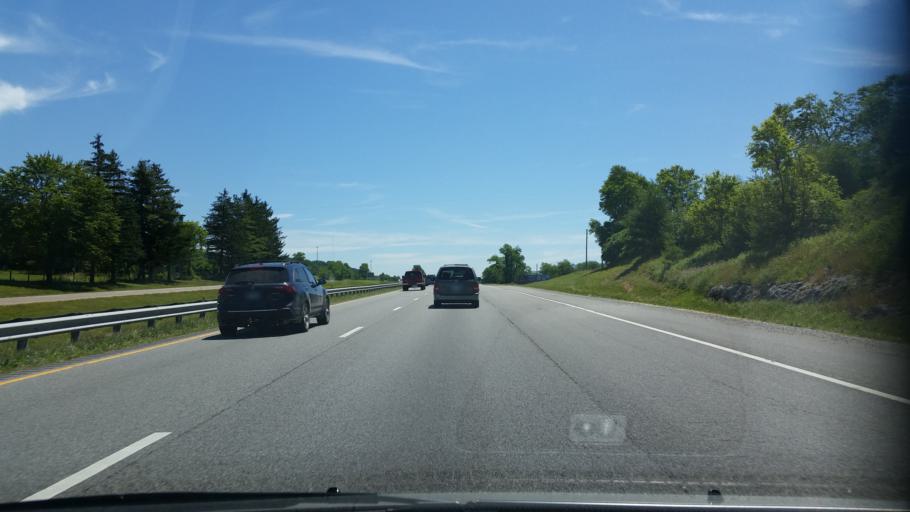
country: US
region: Virginia
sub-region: Wythe County
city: Rural Retreat
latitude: 36.9171
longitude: -81.2600
